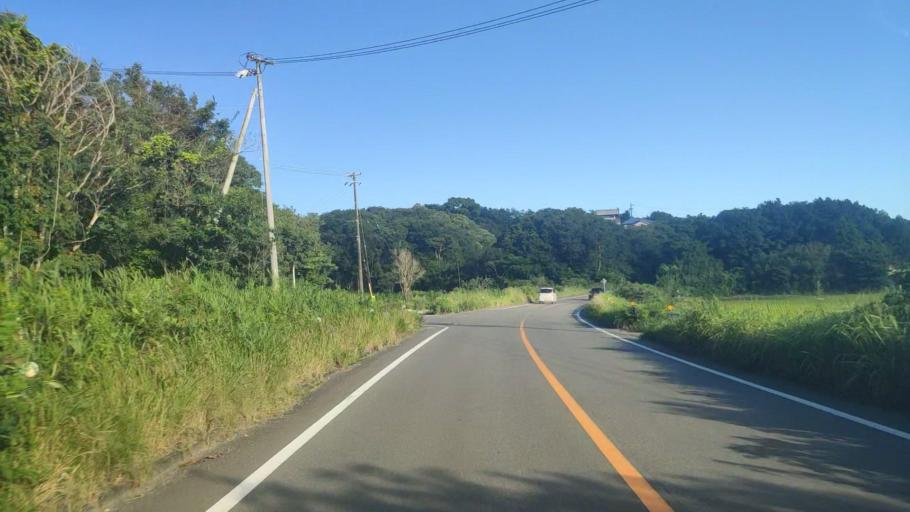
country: JP
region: Mie
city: Toba
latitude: 34.3360
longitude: 136.8407
